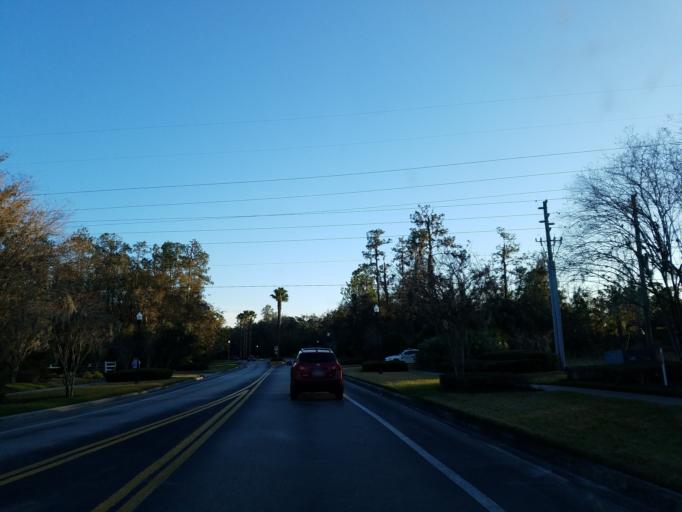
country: US
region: Florida
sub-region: Pasco County
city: Wesley Chapel
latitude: 28.2005
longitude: -82.3654
